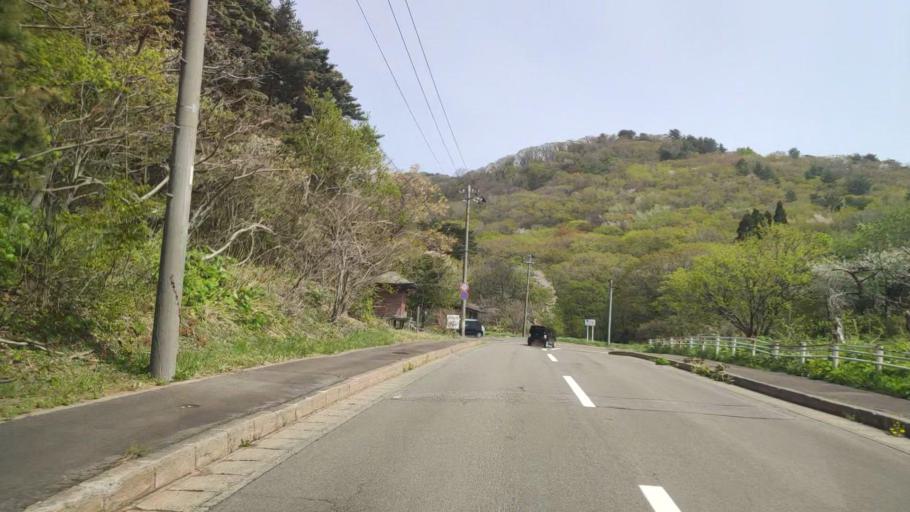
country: JP
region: Aomori
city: Aomori Shi
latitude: 40.9016
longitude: 140.8635
